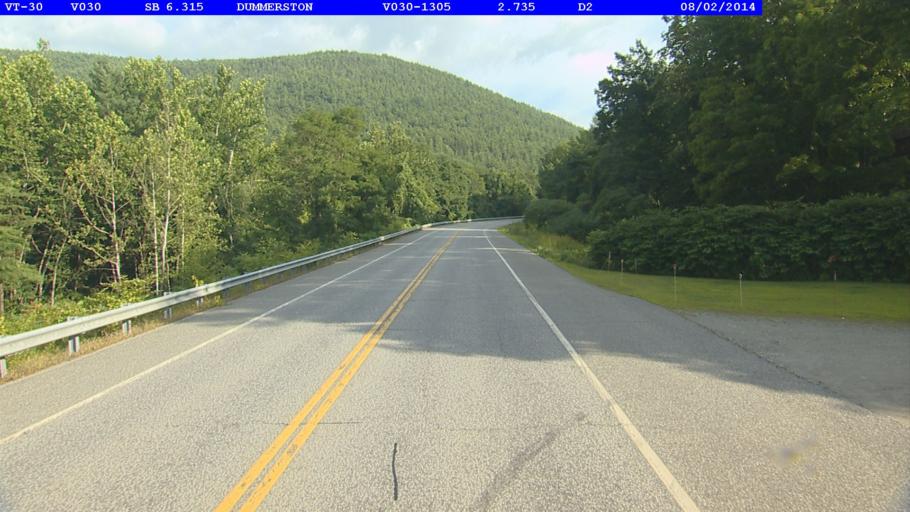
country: US
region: Vermont
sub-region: Windham County
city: Newfane
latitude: 42.9318
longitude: -72.6117
